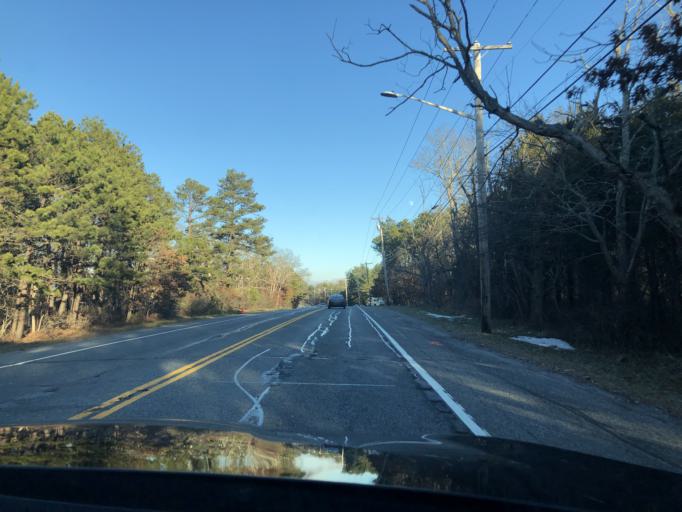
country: US
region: New York
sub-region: Suffolk County
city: Ridge
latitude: 40.9055
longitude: -72.8538
